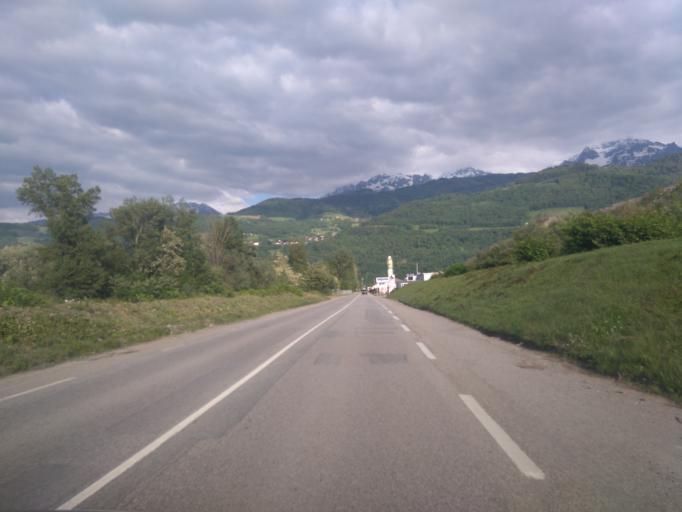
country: FR
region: Rhone-Alpes
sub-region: Departement de l'Isere
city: Saint-Nazaire-les-Eymes
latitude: 45.2364
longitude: 5.8613
